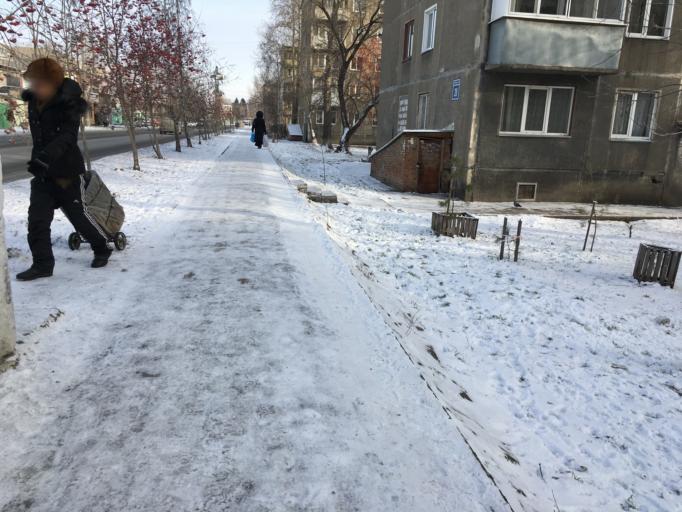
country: RU
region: Novosibirsk
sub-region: Novosibirskiy Rayon
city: Novosibirsk
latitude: 55.0578
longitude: 82.9727
